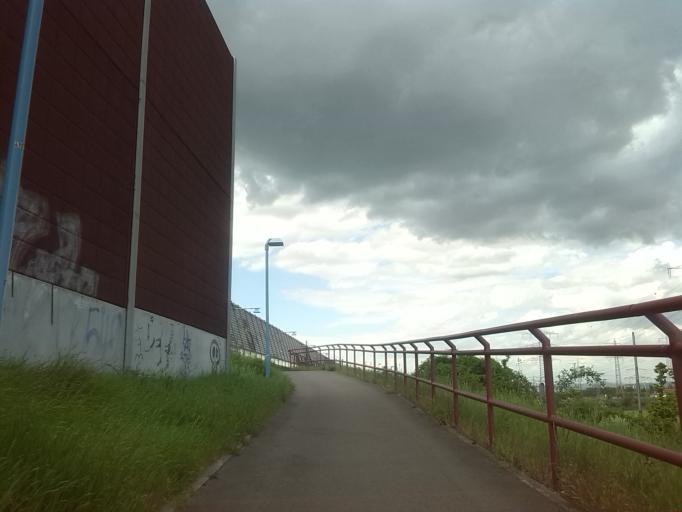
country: DE
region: Baden-Wuerttemberg
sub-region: Karlsruhe Region
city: Ilvesheim
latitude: 49.4739
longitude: 8.5429
